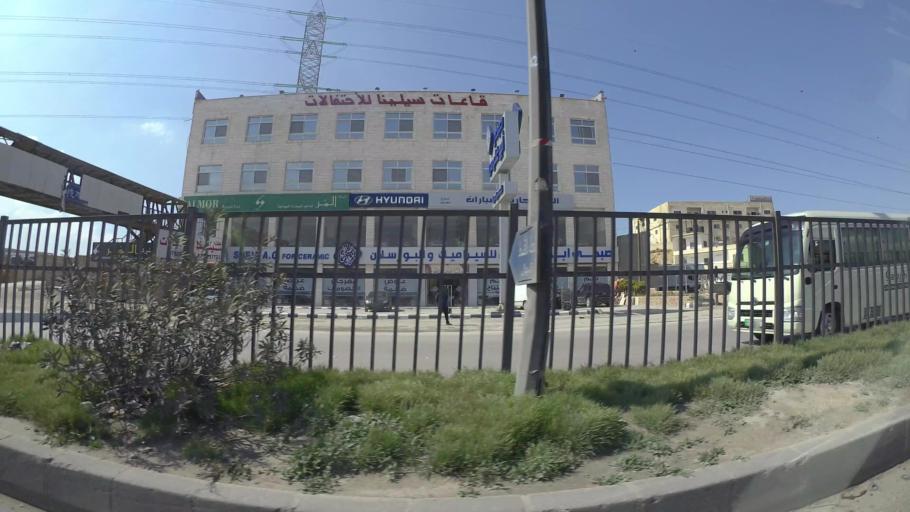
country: JO
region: Zarqa
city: Russeifa
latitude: 32.0023
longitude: 36.0368
